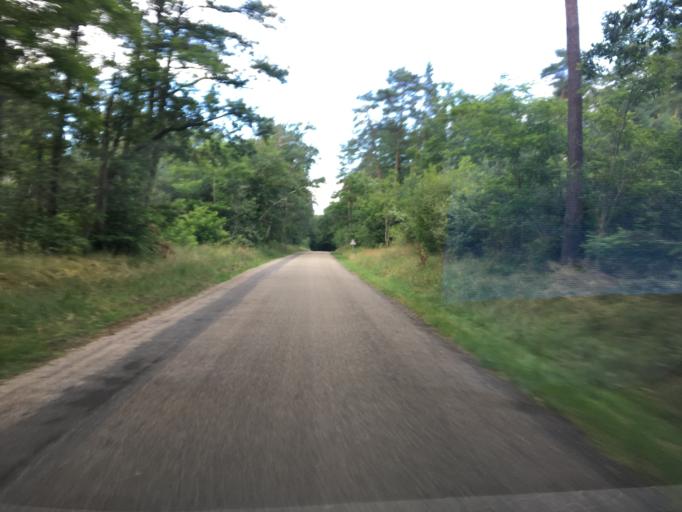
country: FR
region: Bourgogne
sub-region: Departement de l'Yonne
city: Charbuy
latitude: 47.8552
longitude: 3.4868
